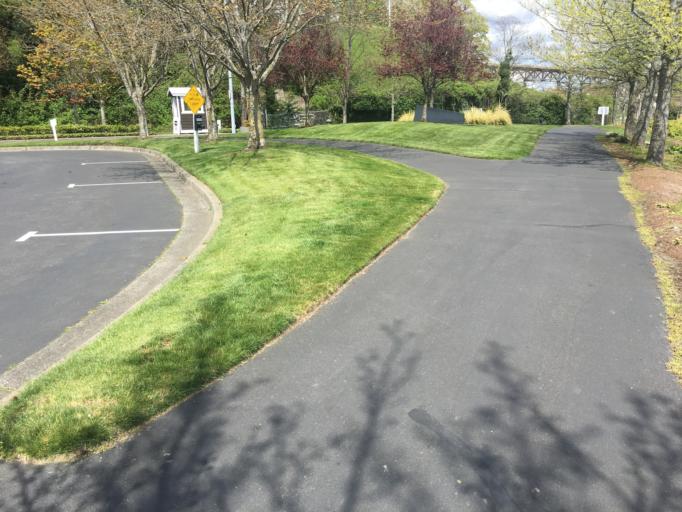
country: US
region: Washington
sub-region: King County
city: Seattle
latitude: 47.6310
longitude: -122.3888
